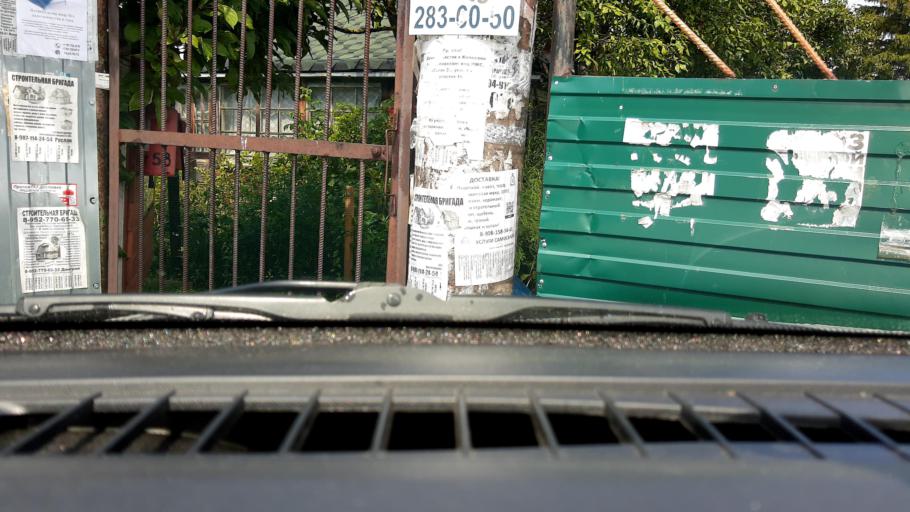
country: RU
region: Nizjnij Novgorod
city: Gorbatovka
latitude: 56.3831
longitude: 43.8221
